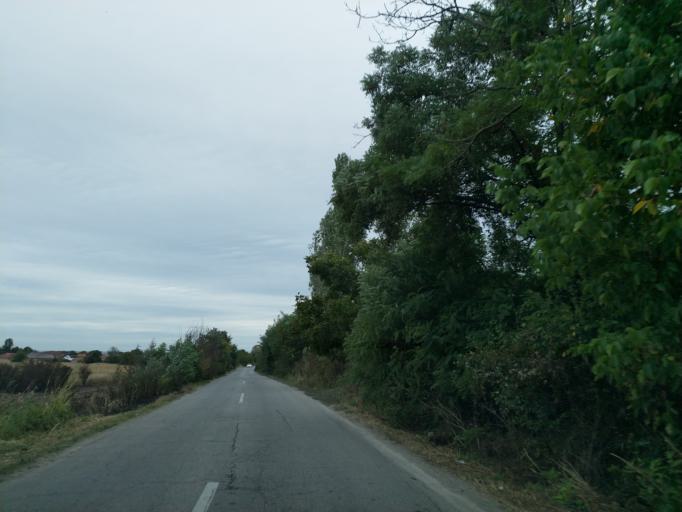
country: RS
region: Central Serbia
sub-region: Pomoravski Okrug
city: Paracin
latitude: 43.8485
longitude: 21.3221
